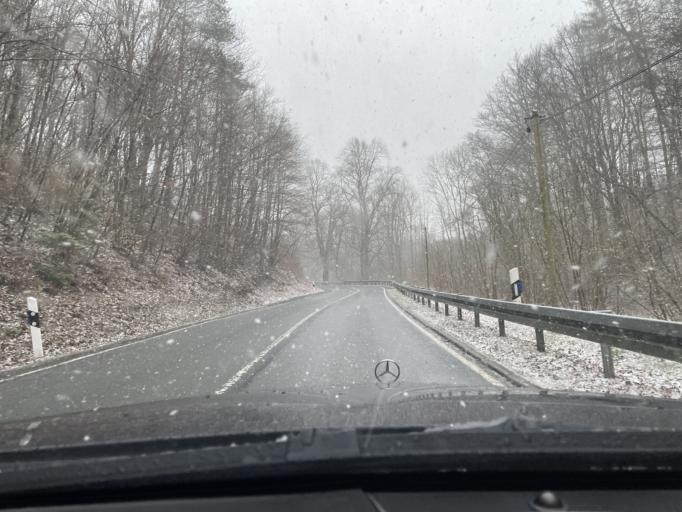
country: DE
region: Thuringia
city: Effelder
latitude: 51.2465
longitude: 10.2454
